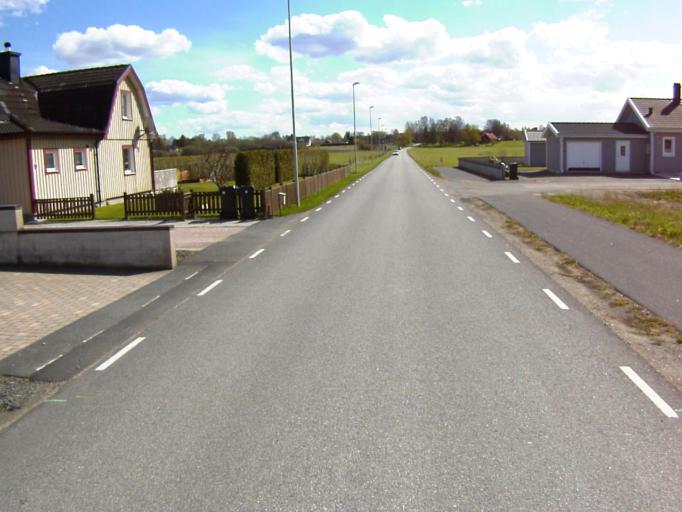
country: SE
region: Skane
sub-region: Kristianstads Kommun
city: Kristianstad
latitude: 56.0157
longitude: 14.0904
